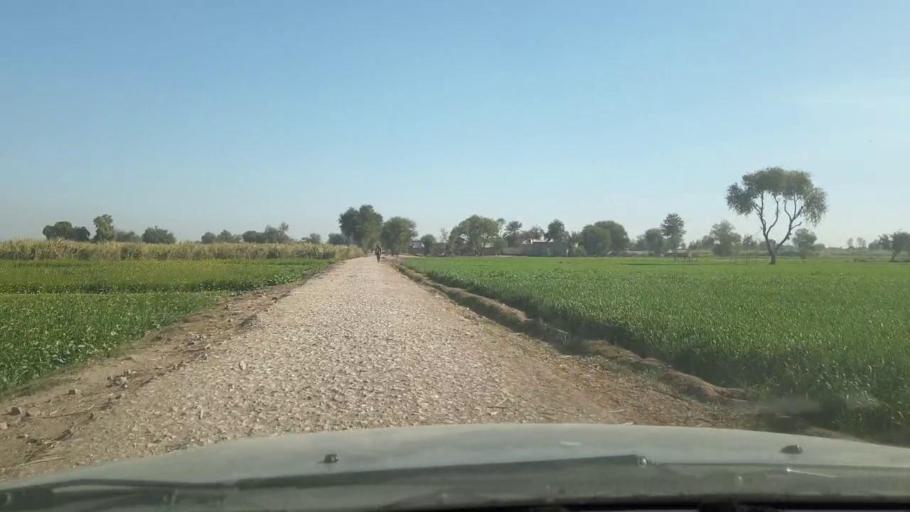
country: PK
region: Sindh
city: Ghotki
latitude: 27.9739
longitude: 69.1899
